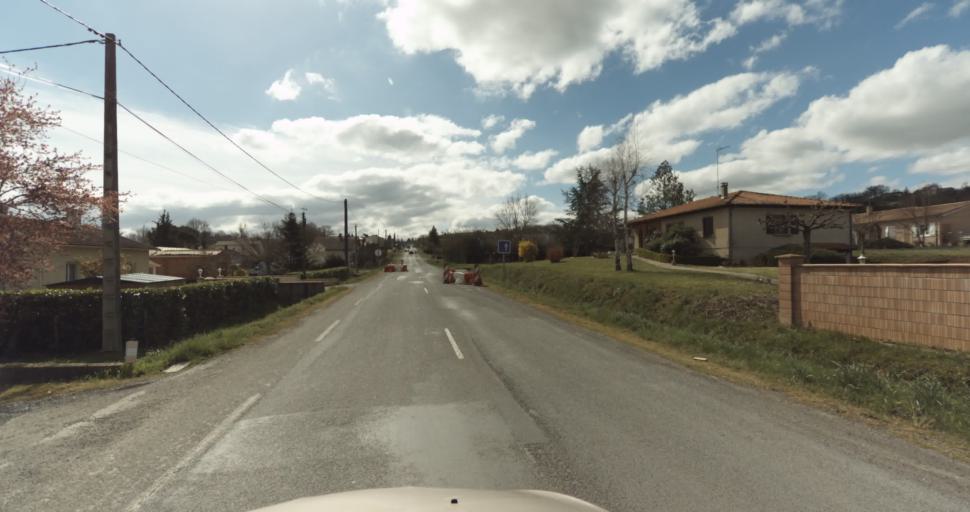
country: FR
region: Midi-Pyrenees
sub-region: Departement du Tarn
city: Puygouzon
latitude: 43.8914
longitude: 2.1526
